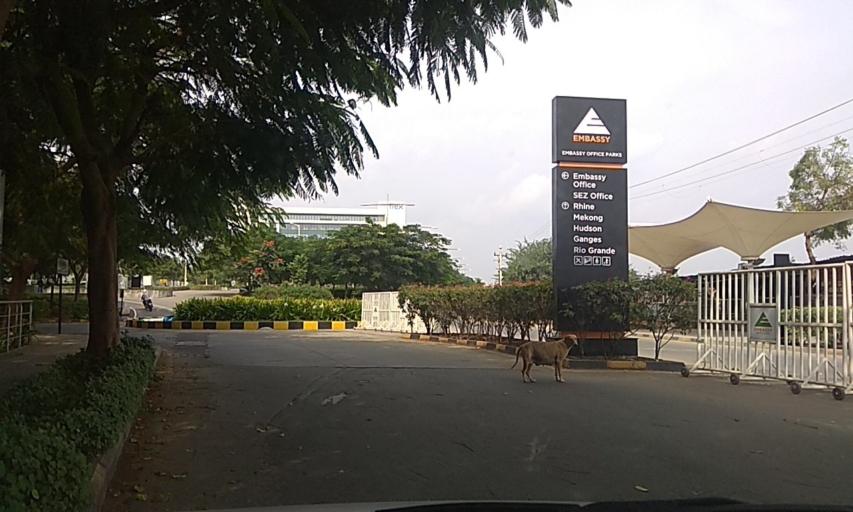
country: IN
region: Maharashtra
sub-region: Pune Division
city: Pimpri
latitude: 18.6036
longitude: 73.7170
